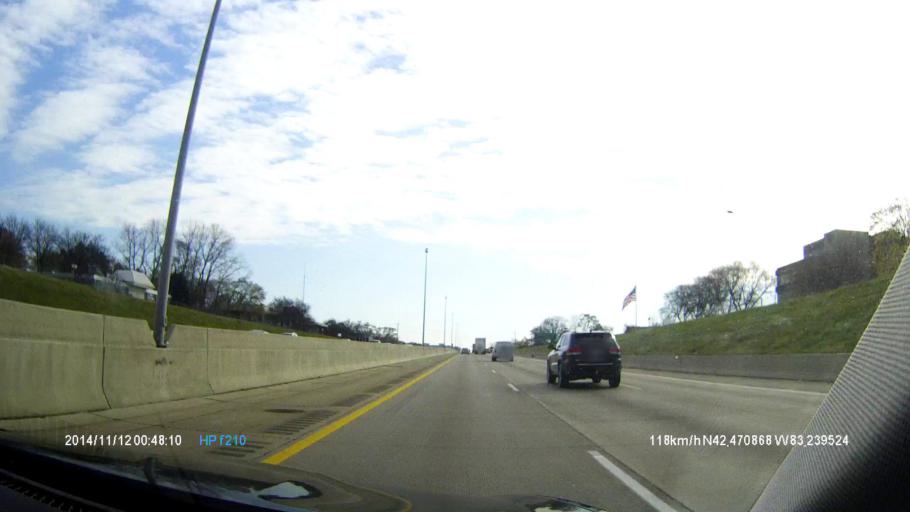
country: US
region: Michigan
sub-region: Oakland County
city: Southfield
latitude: 42.4707
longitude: -83.2393
